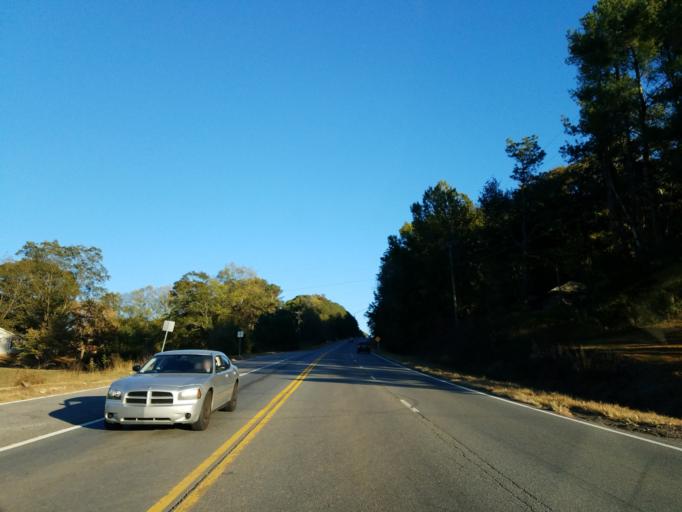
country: US
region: Georgia
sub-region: Dawson County
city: Dawsonville
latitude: 34.3811
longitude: -84.0604
